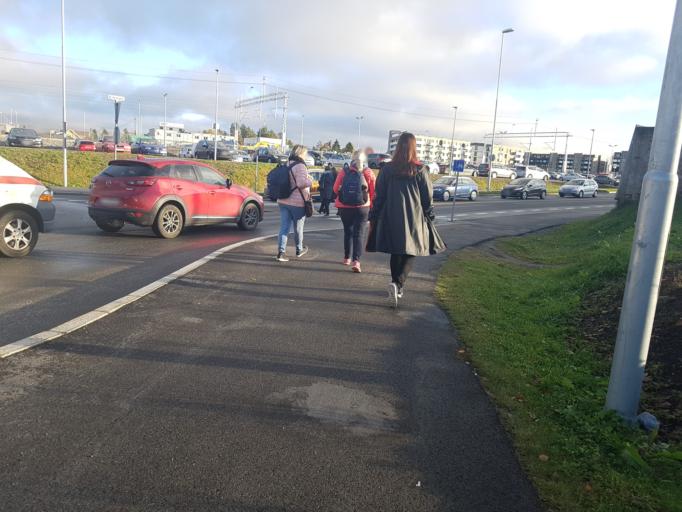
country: NO
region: Akershus
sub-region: Ullensaker
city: Jessheim
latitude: 60.1445
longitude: 11.1765
